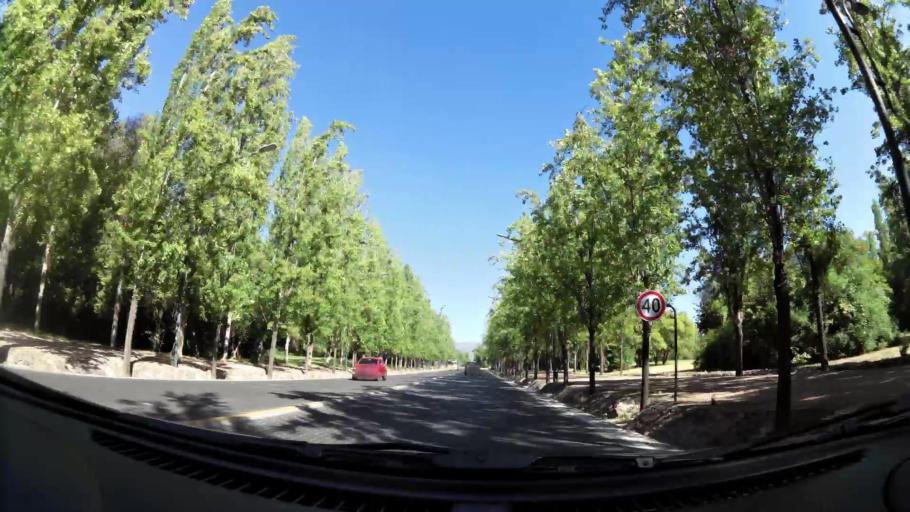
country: AR
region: Mendoza
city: Mendoza
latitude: -32.8848
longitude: -68.8710
